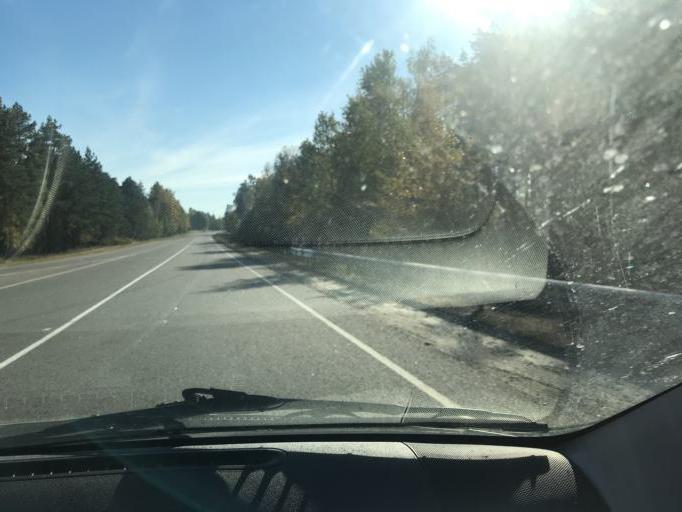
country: BY
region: Brest
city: Mikashevichy
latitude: 52.2413
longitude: 27.4458
